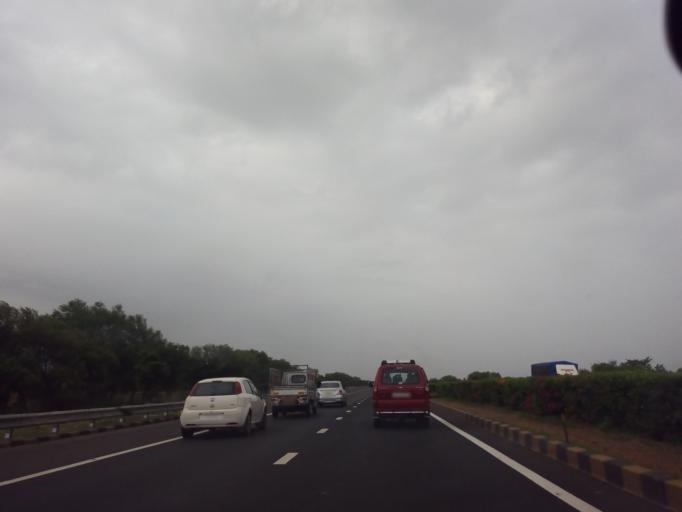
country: IN
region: Gujarat
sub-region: Kheda
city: Mahemdavad
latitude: 22.8462
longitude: 72.8162
